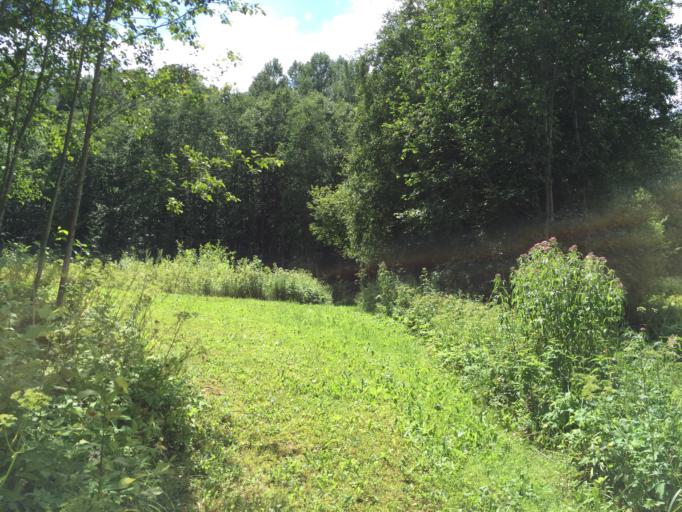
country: LV
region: Ropazu
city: Ropazi
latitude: 56.9082
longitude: 24.7742
